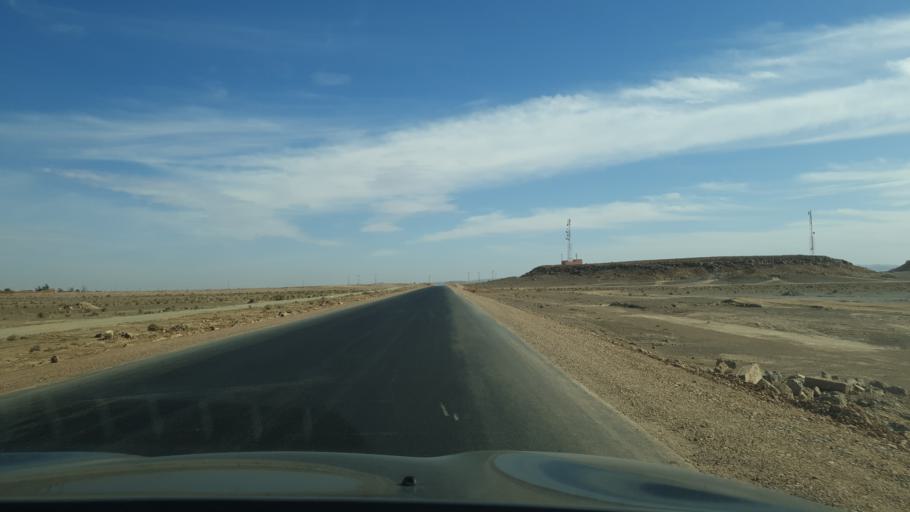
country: MA
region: Meknes-Tafilalet
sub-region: Errachidia
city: Goulmima
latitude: 31.4845
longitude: -5.1369
